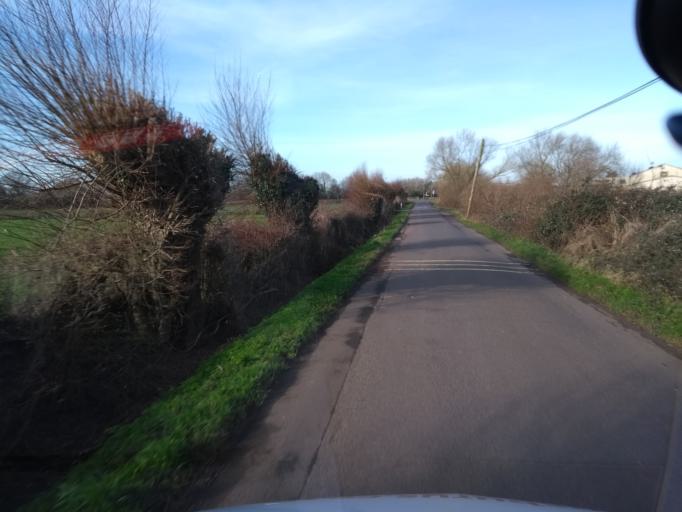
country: GB
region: England
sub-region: Somerset
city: Creech Saint Michael
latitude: 51.0210
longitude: -3.0358
